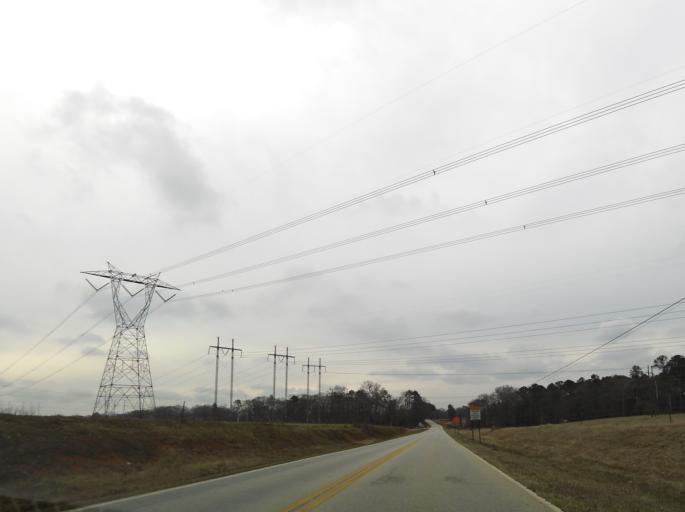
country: US
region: Georgia
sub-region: Houston County
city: Robins Air Force Base
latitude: 32.5591
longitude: -83.5864
